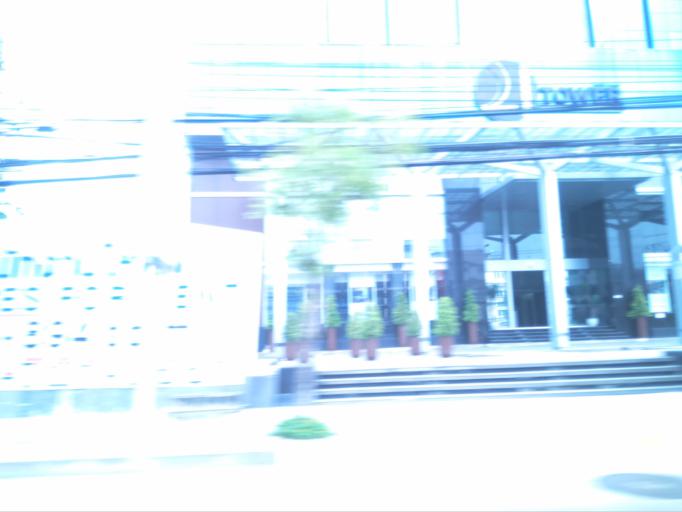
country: TH
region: Bangkok
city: Suan Luang
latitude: 13.7220
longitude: 100.6421
